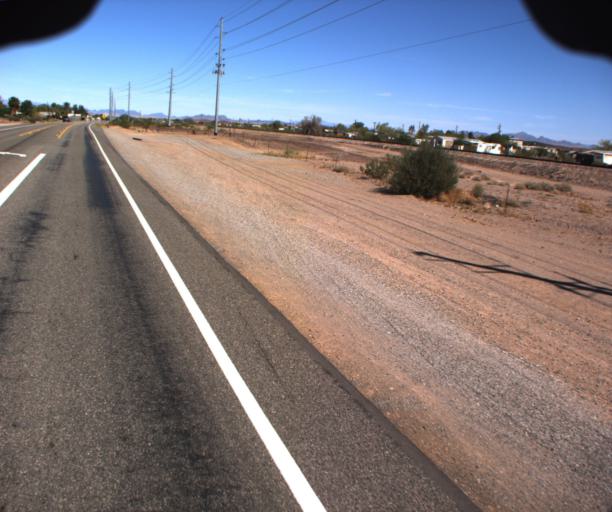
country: US
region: Arizona
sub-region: La Paz County
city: Cienega Springs
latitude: 33.9271
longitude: -114.0016
